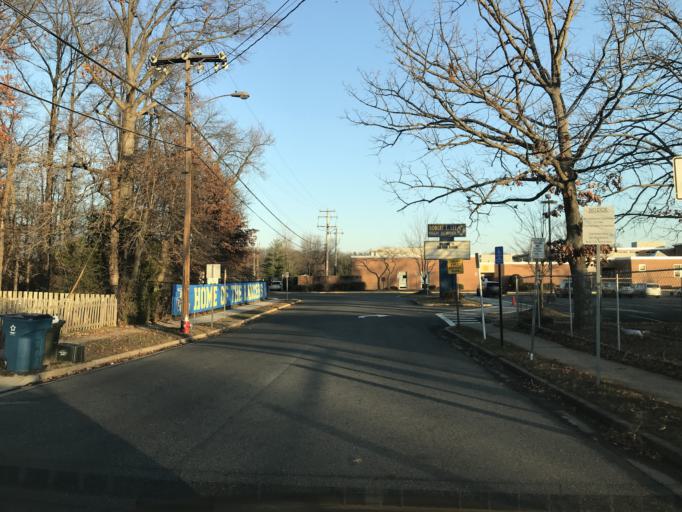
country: US
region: Virginia
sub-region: Fairfax County
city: Springfield
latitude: 38.7815
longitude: -77.1715
